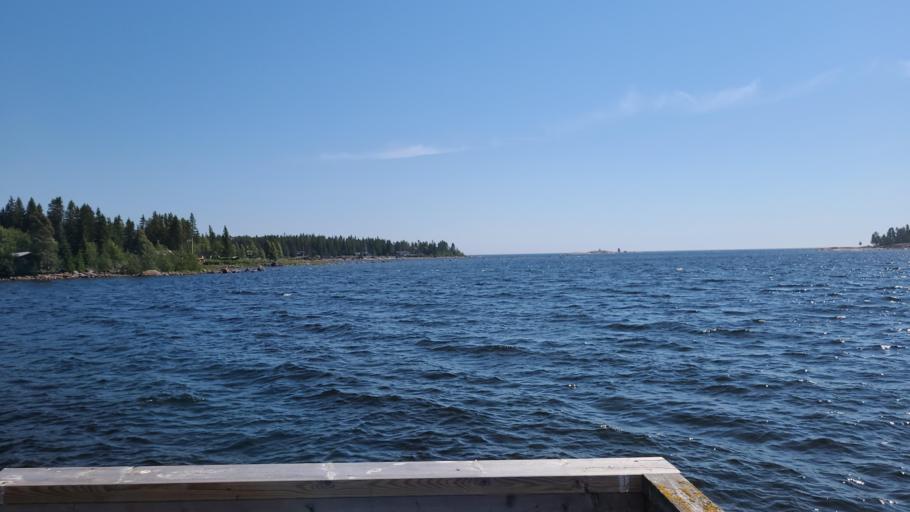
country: SE
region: Vaesterbotten
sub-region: Robertsfors Kommun
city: Robertsfors
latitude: 64.1424
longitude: 20.9666
